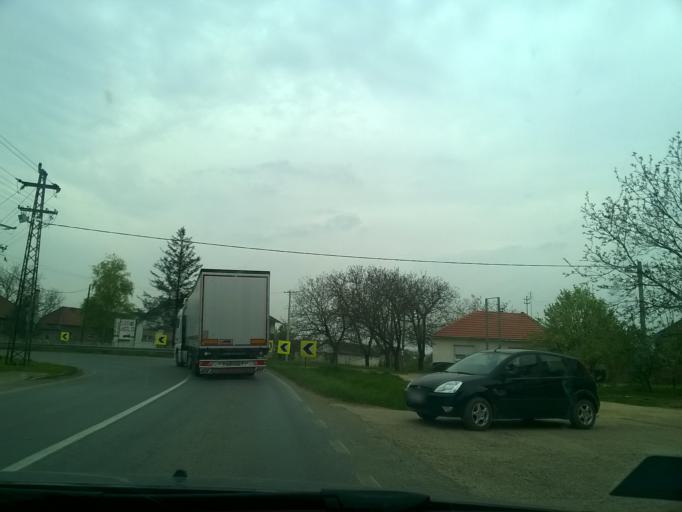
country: RS
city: Hrtkovci
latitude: 44.8815
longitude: 19.7630
